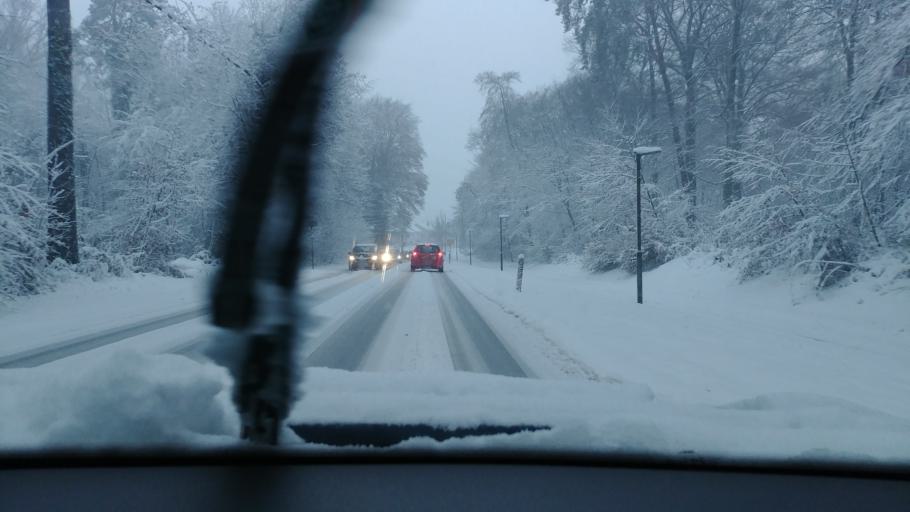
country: DE
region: North Rhine-Westphalia
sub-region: Regierungsbezirk Koln
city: Bergisch Gladbach
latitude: 50.9685
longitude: 7.1174
